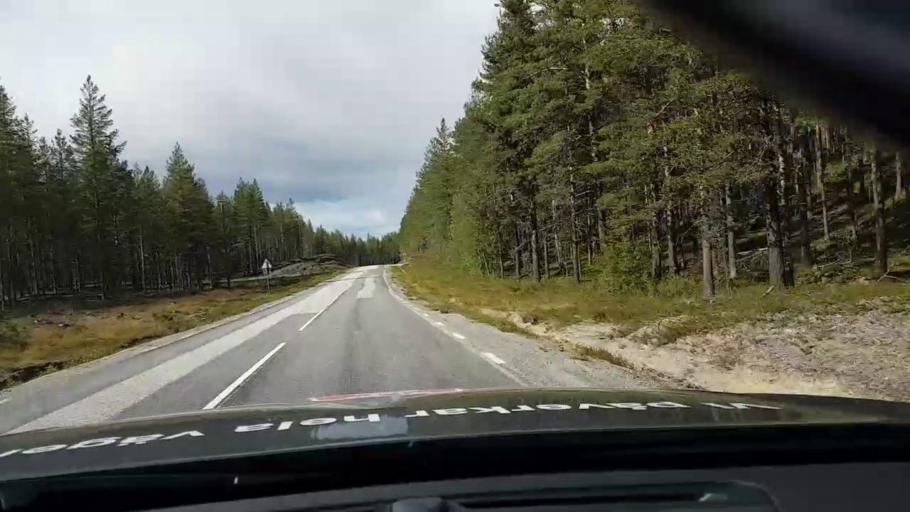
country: SE
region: Vaesterbotten
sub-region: Asele Kommun
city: Asele
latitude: 63.8546
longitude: 17.3894
